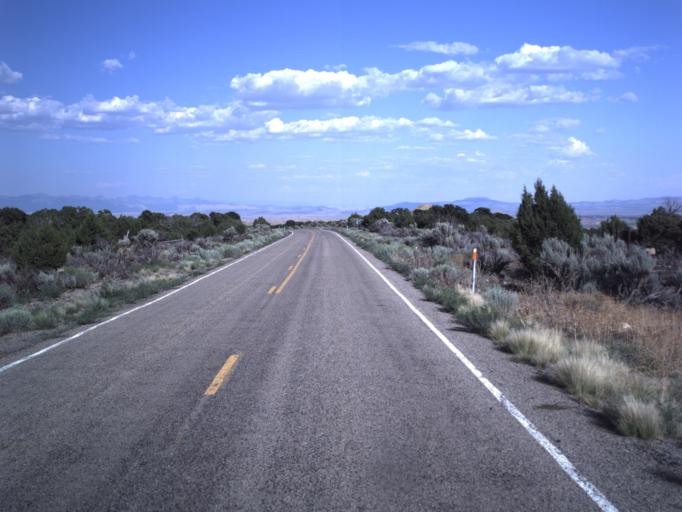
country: US
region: Utah
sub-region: Emery County
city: Huntington
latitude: 39.4857
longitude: -110.9342
